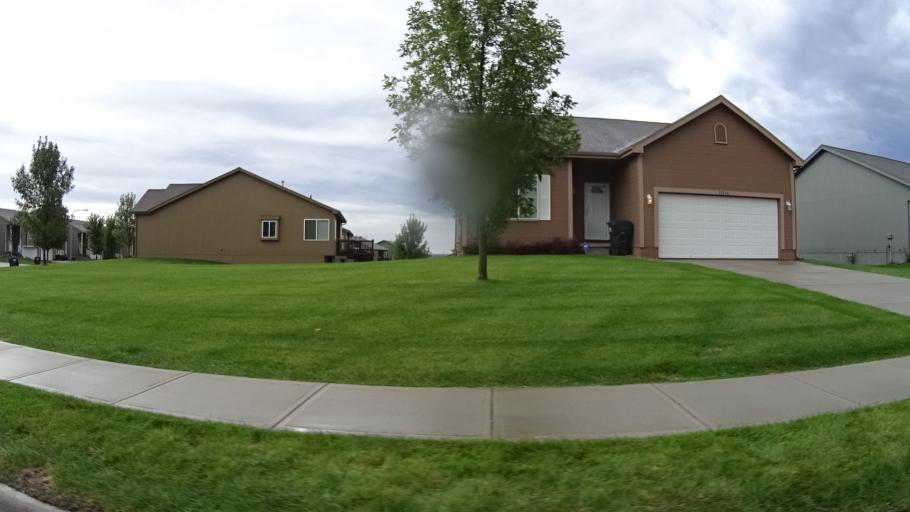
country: US
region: Nebraska
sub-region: Sarpy County
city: Offutt Air Force Base
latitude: 41.1561
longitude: -95.9489
